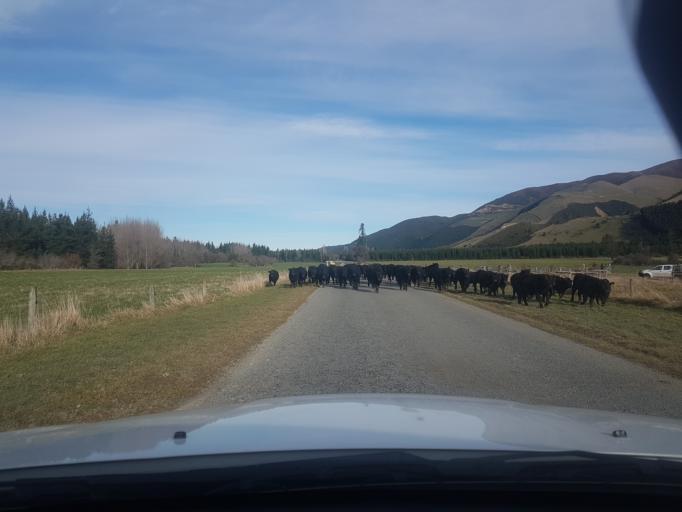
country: NZ
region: Canterbury
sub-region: Timaru District
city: Pleasant Point
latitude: -43.8415
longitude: 171.2540
